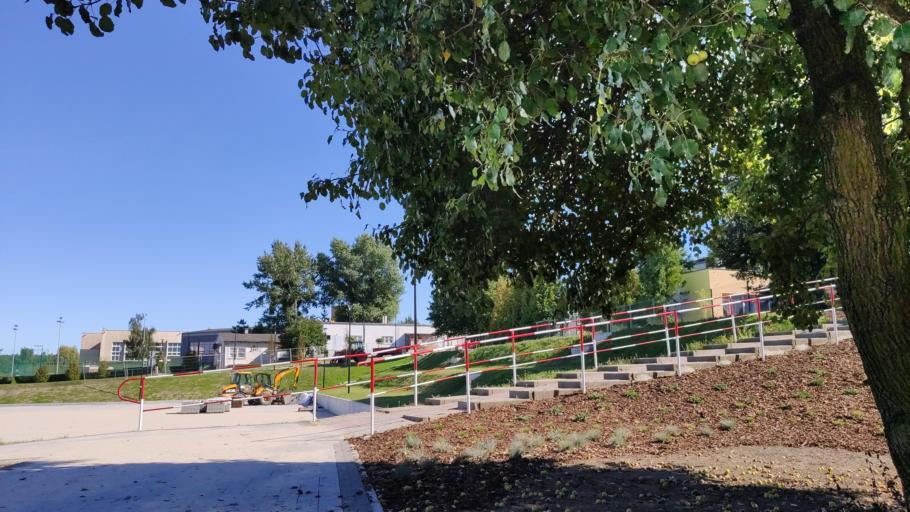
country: PL
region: Kujawsko-Pomorskie
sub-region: Powiat zninski
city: Barcin
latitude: 52.8554
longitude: 17.9408
